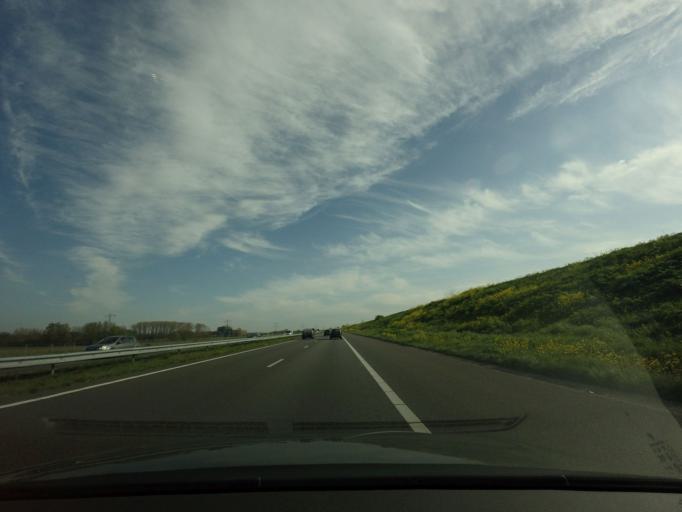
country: NL
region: North Brabant
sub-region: Gemeente Bernheze
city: Heesch
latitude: 51.7094
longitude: 5.5704
